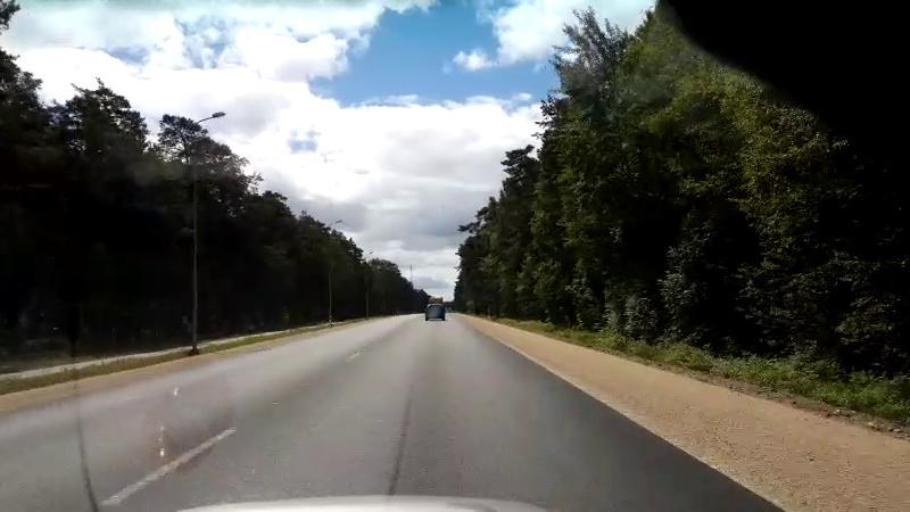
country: LV
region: Salacgrivas
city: Salacgriva
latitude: 57.7725
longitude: 24.3554
